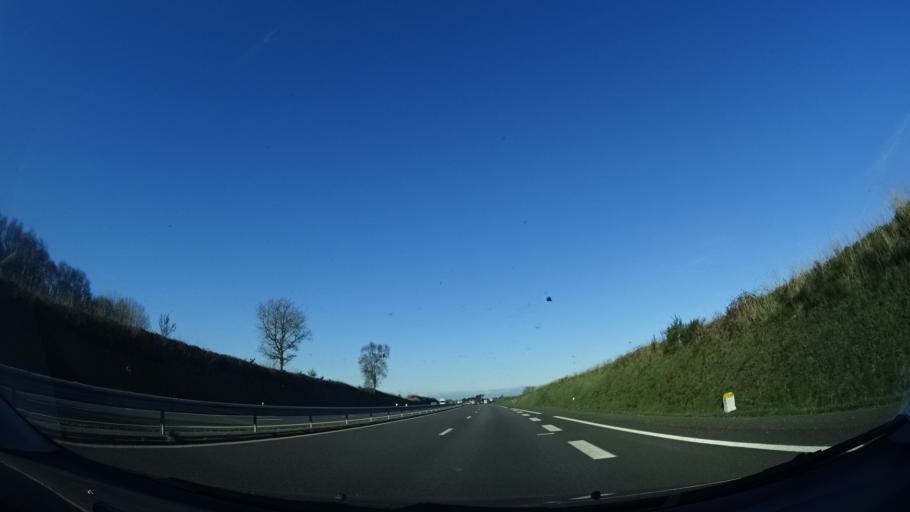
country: FR
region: Brittany
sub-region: Departement du Finistere
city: Taule
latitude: 48.6078
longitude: -3.8884
